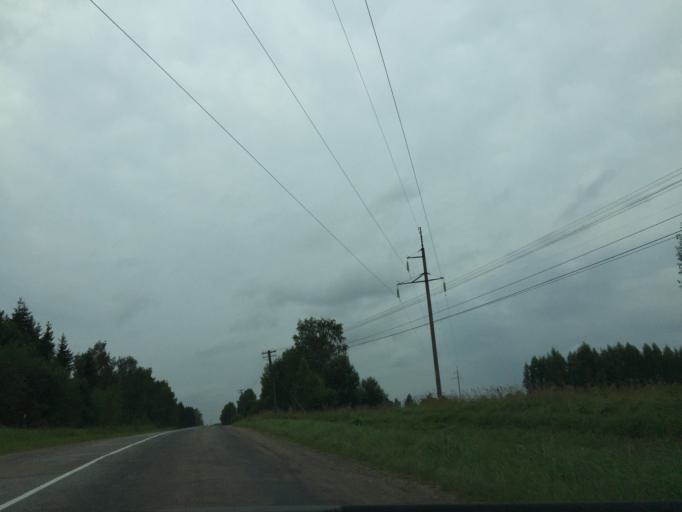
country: LV
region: Zilupes
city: Zilupe
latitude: 56.3878
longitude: 28.0975
